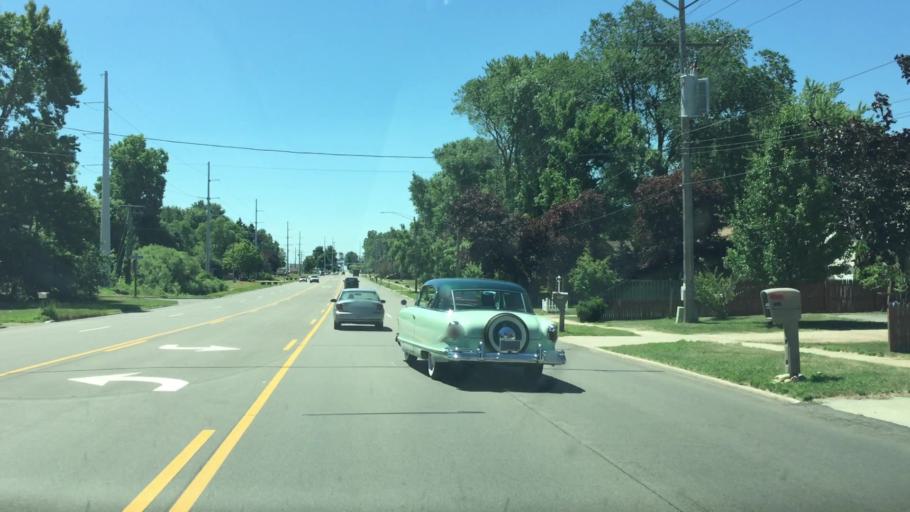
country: US
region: Wisconsin
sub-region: Winnebago County
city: Menasha
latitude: 44.2175
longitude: -88.4043
